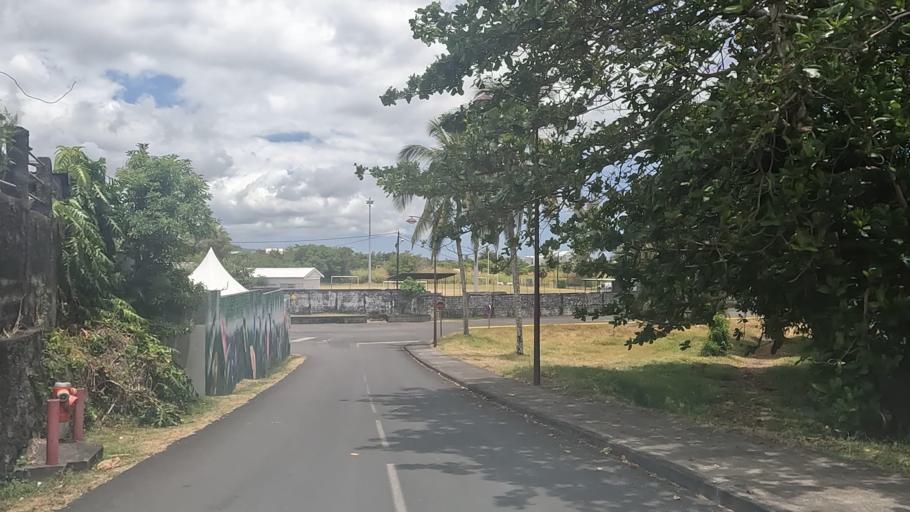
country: RE
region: Reunion
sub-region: Reunion
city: Saint-Benoit
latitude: -21.0354
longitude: 55.7171
